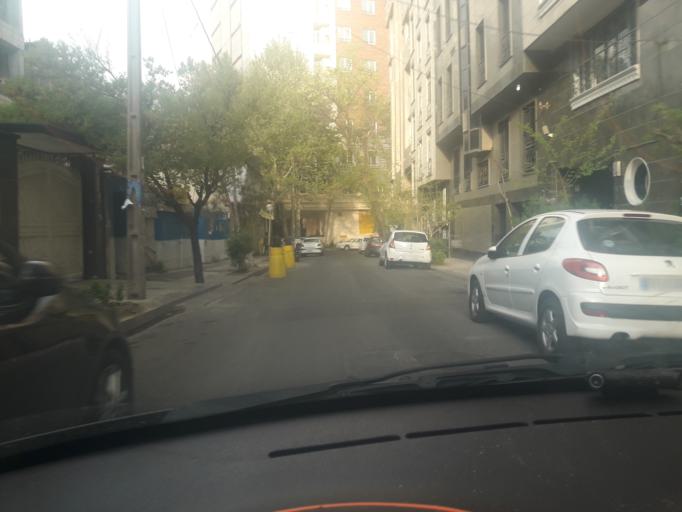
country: IR
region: Tehran
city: Tehran
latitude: 35.7382
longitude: 51.4068
